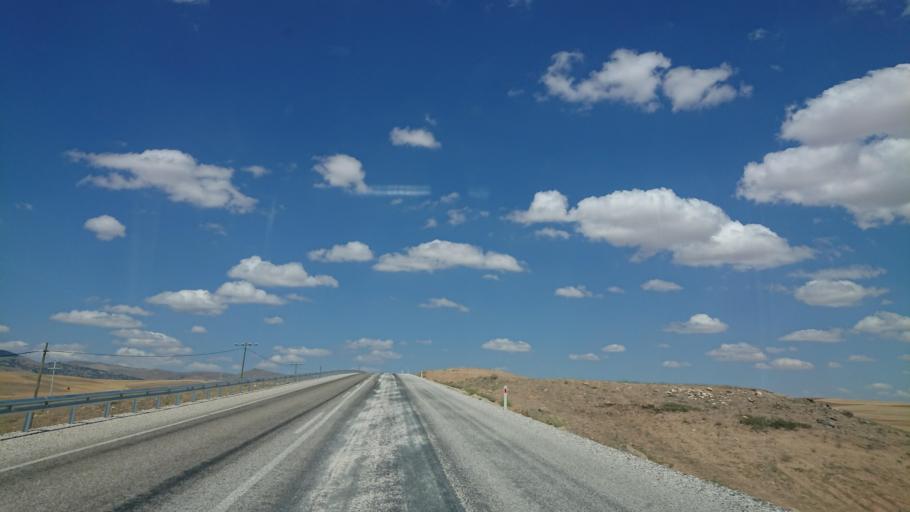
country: TR
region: Ankara
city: Evren
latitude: 39.1077
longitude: 33.9243
